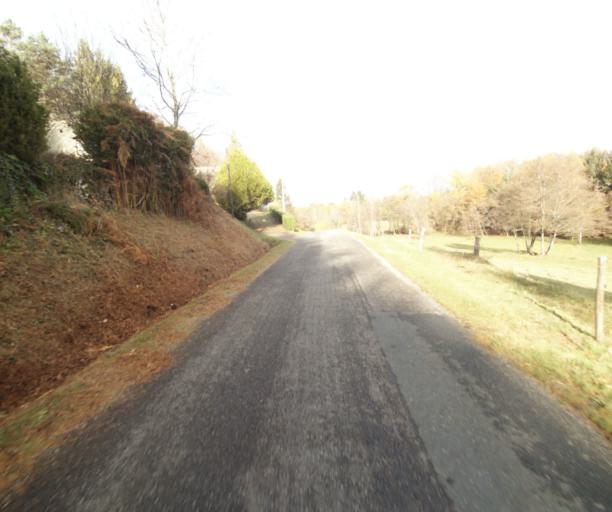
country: FR
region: Limousin
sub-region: Departement de la Correze
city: Sainte-Fortunade
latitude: 45.1919
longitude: 1.7383
